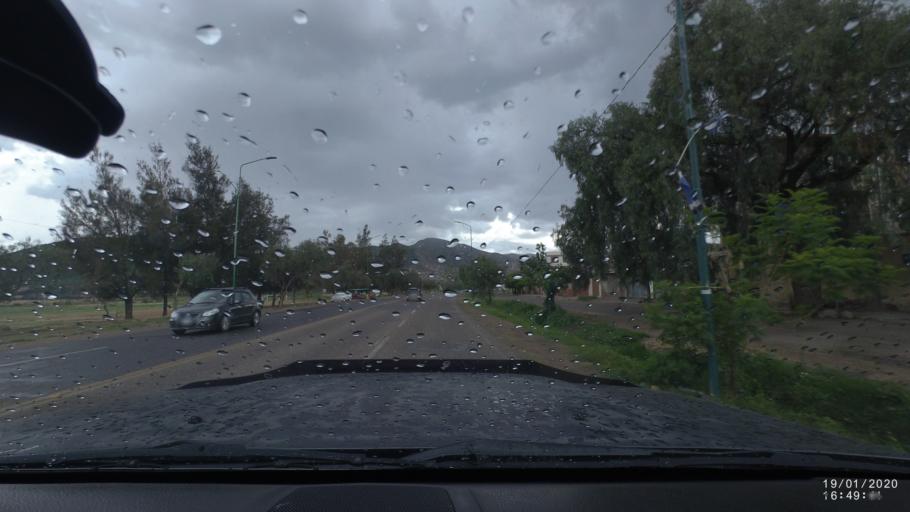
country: BO
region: Cochabamba
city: Cochabamba
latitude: -17.4170
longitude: -66.1388
